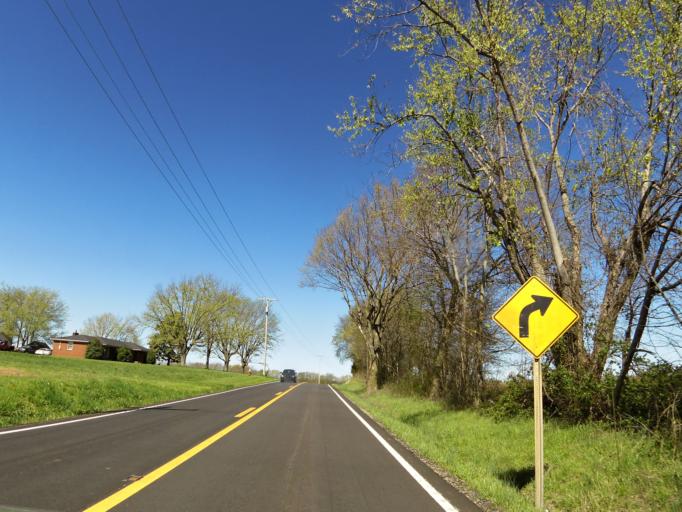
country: US
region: Tennessee
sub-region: Robertson County
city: Springfield
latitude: 36.5662
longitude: -86.8519
